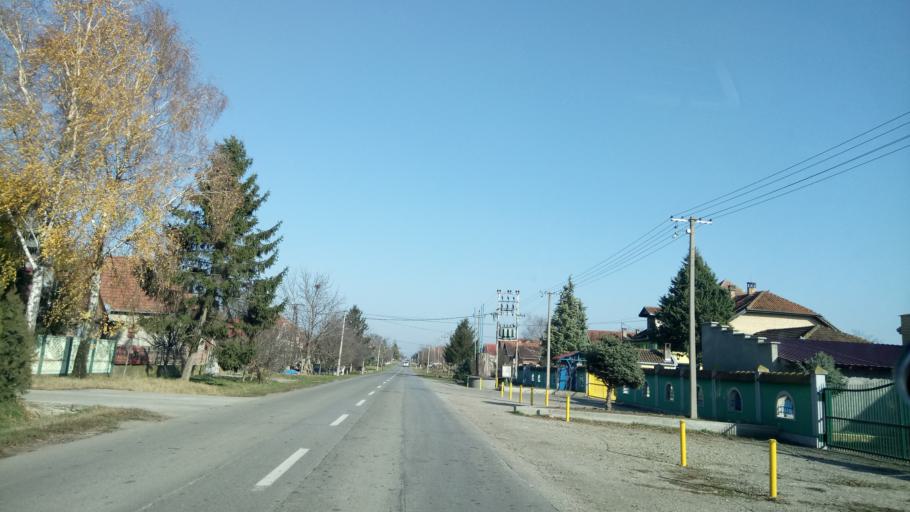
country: RS
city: Ljukovo
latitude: 45.0159
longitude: 20.0264
